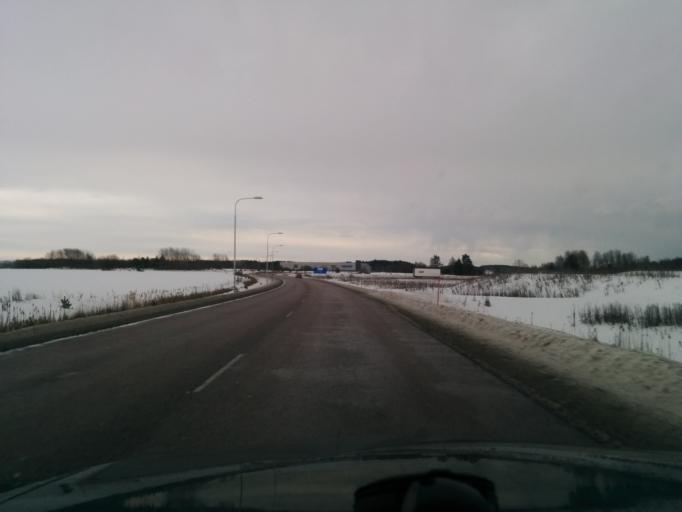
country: SE
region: Vaestmanland
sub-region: Vasteras
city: Vasteras
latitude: 59.5920
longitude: 16.4390
